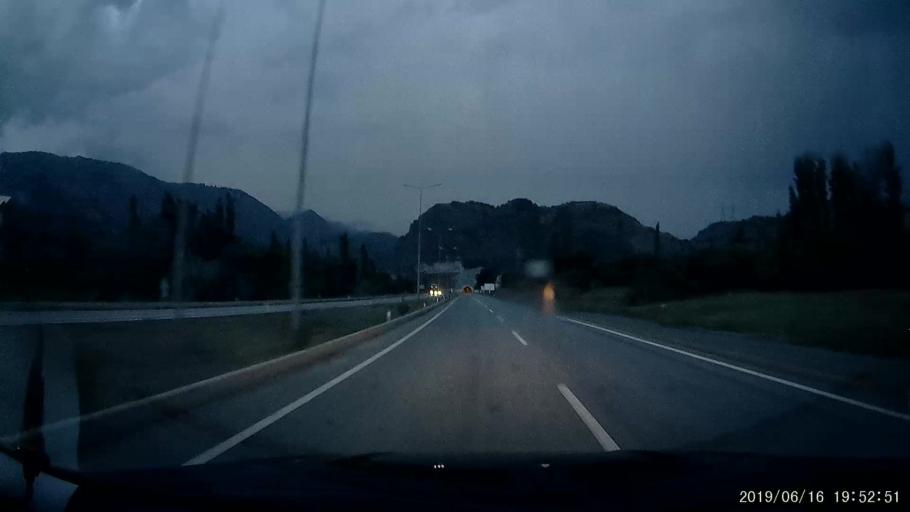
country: TR
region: Sivas
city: Koyulhisar
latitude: 40.2890
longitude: 37.7961
